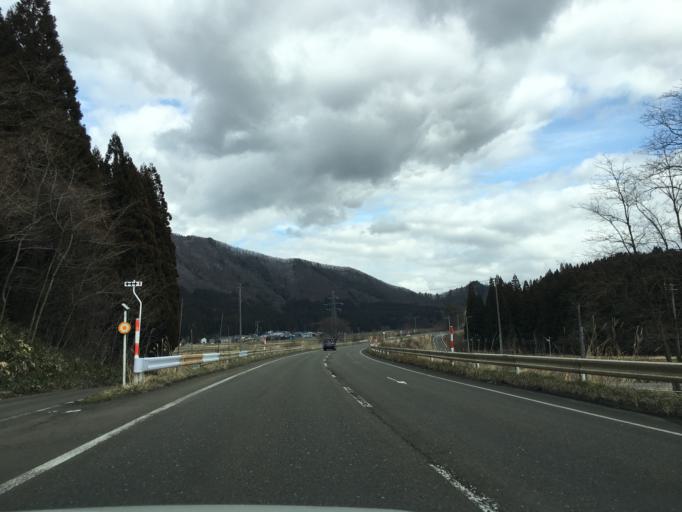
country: JP
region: Akita
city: Odate
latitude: 40.2208
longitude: 140.6503
